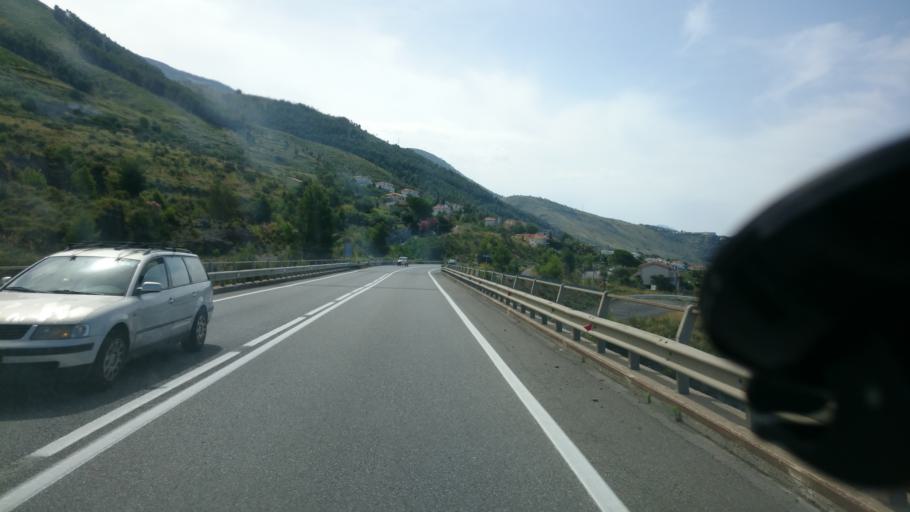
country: IT
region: Calabria
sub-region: Provincia di Cosenza
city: Praia a Mare
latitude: 39.8915
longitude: 15.7906
